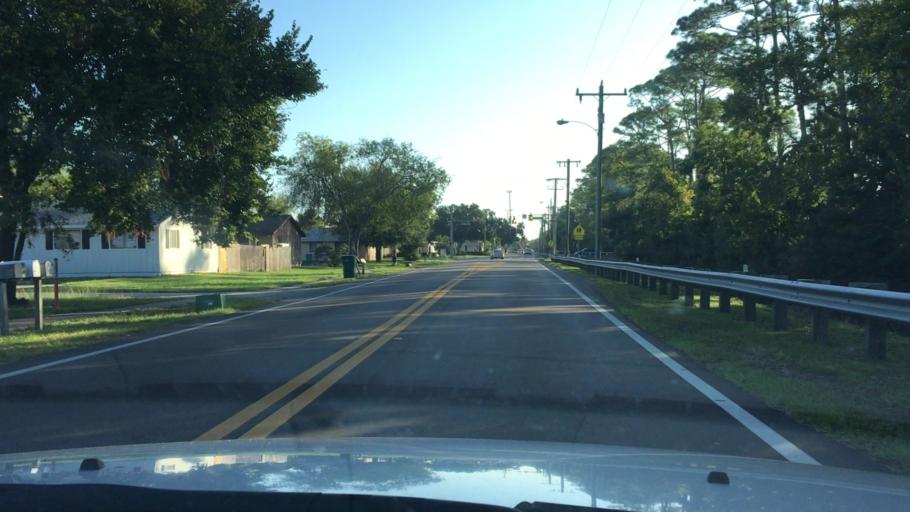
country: US
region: Florida
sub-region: Volusia County
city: Holly Hill
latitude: 29.2417
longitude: -81.0516
